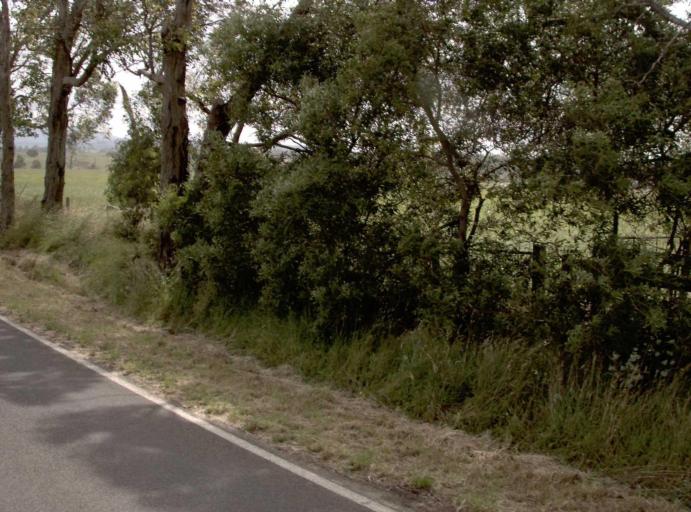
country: AU
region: Victoria
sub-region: Latrobe
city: Moe
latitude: -38.1458
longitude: 146.1465
